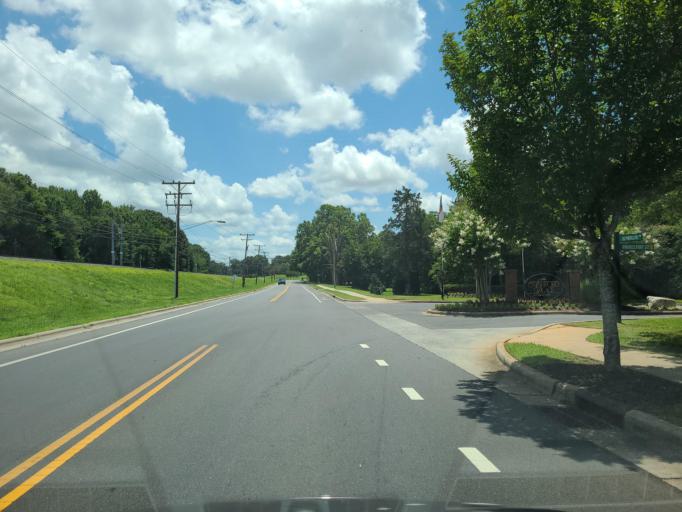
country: US
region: North Carolina
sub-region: Mecklenburg County
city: Pineville
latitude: 35.1495
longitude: -80.8786
